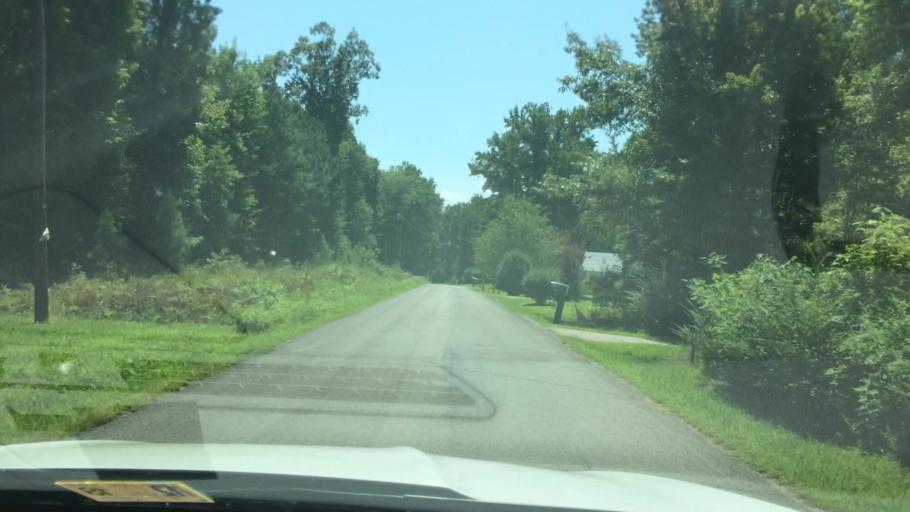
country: US
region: Virginia
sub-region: Charles City County
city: Charles City
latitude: 37.2926
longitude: -76.9654
